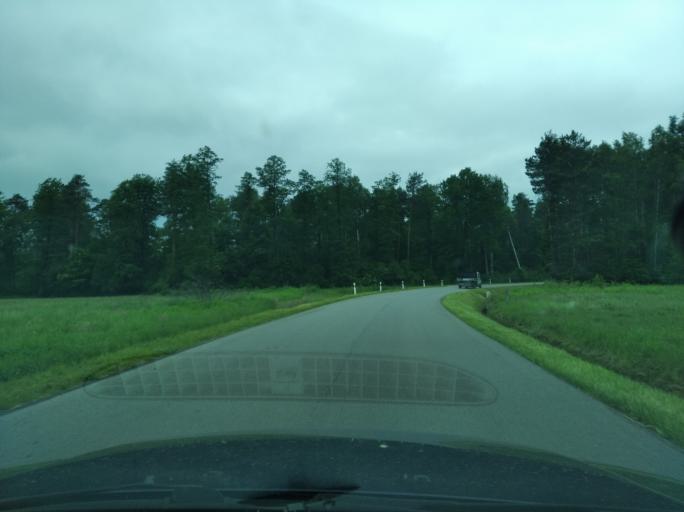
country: PL
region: Subcarpathian Voivodeship
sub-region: Powiat kolbuszowski
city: Niwiska
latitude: 50.1817
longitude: 21.6575
